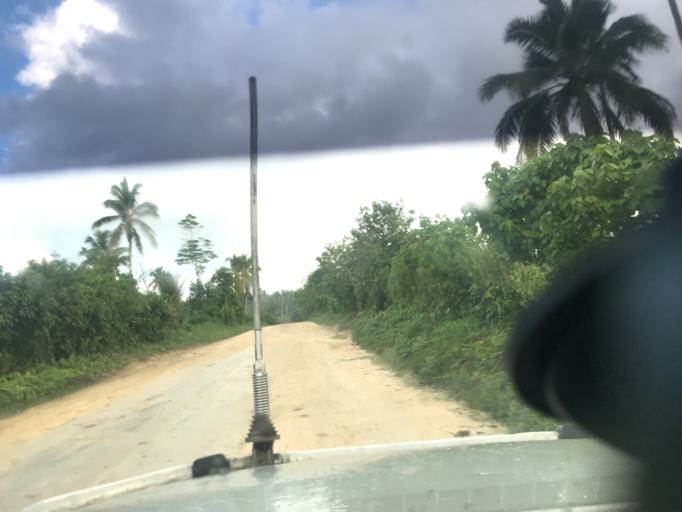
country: SB
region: Malaita
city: Auki
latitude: -8.6472
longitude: 160.6678
